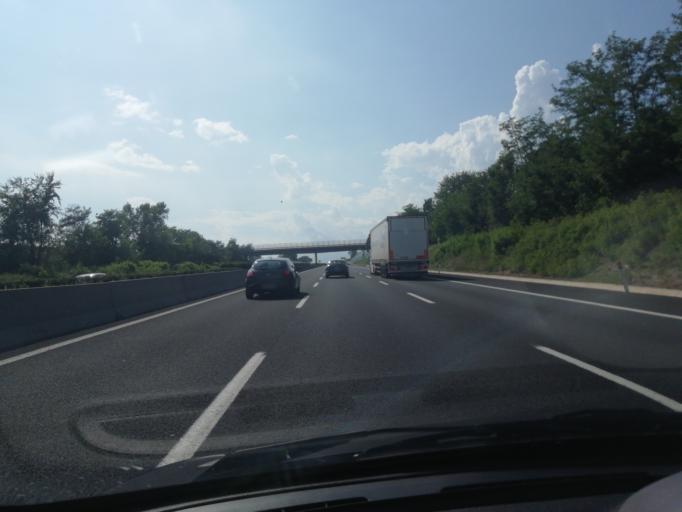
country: IT
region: Latium
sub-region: Provincia di Frosinone
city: Pofi
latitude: 41.5526
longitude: 13.4432
